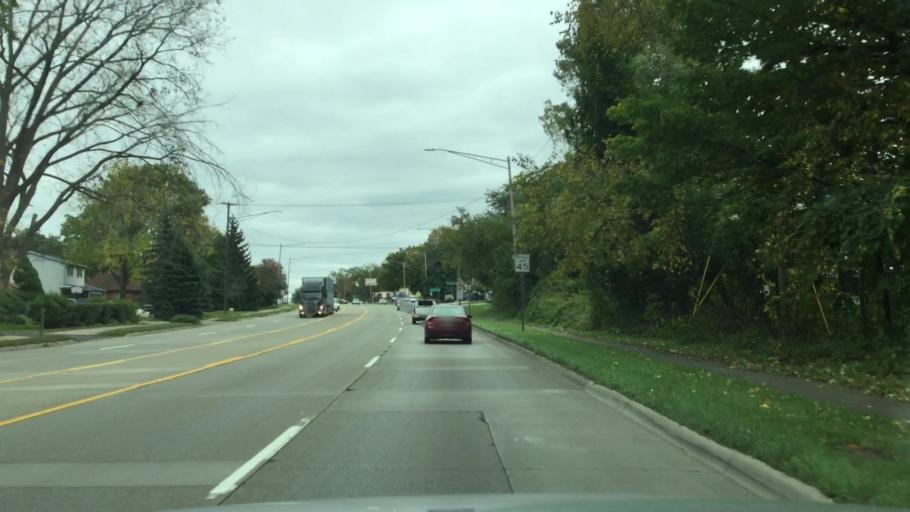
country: US
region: Michigan
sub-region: Oakland County
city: Keego Harbor
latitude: 42.6353
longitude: -83.3431
